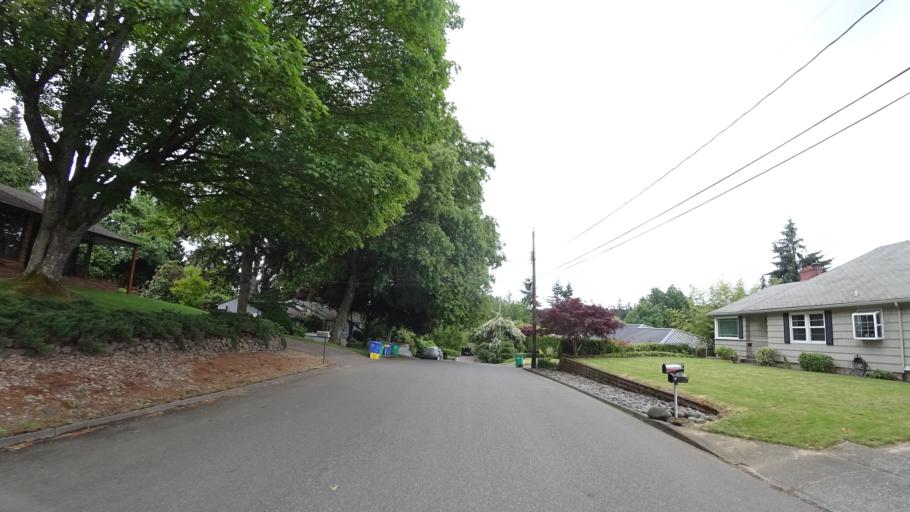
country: US
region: Oregon
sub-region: Clackamas County
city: Lake Oswego
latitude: 45.4615
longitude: -122.6993
